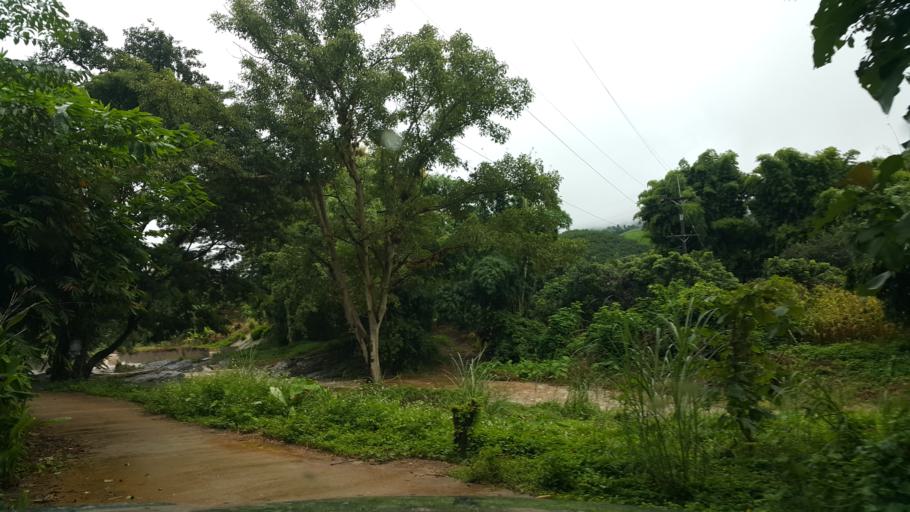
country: TH
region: Phayao
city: Chiang Kham
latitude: 19.4974
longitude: 100.4601
